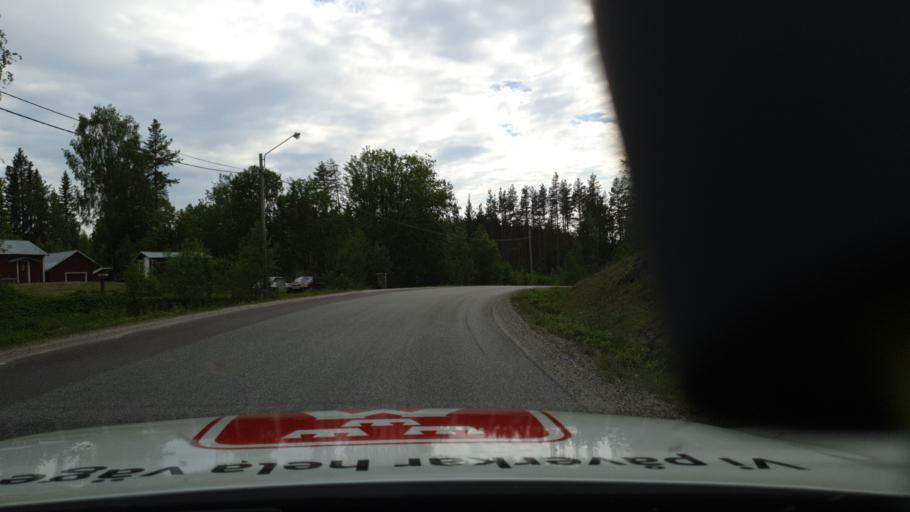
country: SE
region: Jaemtland
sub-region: Braecke Kommun
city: Braecke
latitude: 63.0421
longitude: 15.2865
